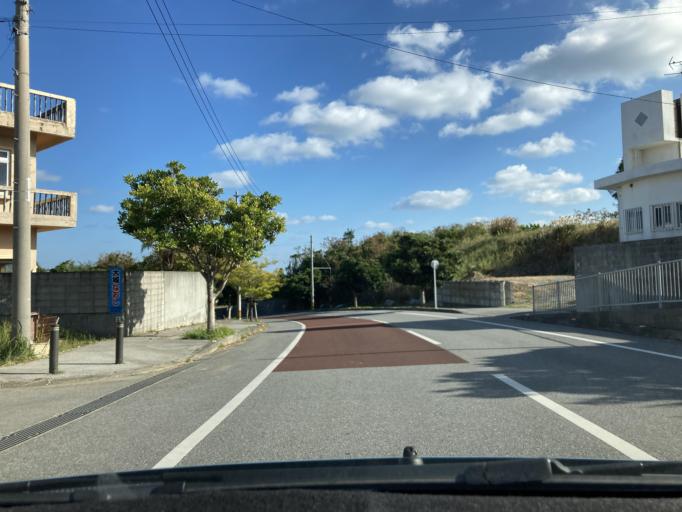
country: JP
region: Okinawa
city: Katsuren-haebaru
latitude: 26.3052
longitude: 127.9156
